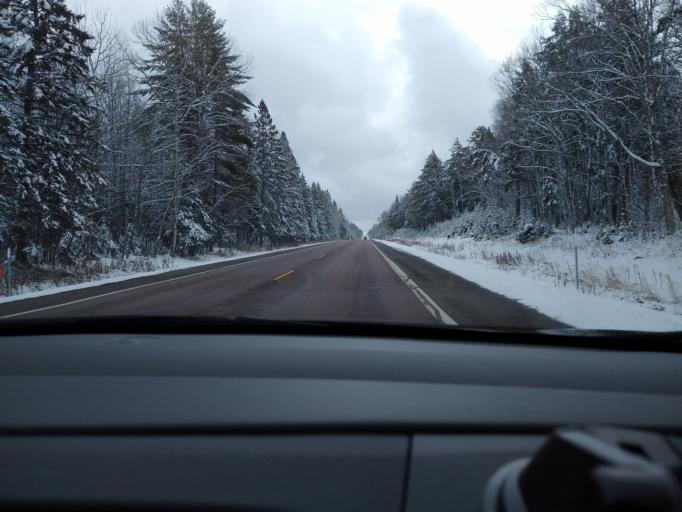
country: US
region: Wisconsin
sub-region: Vilas County
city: Eagle River
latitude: 46.2145
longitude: -89.0429
